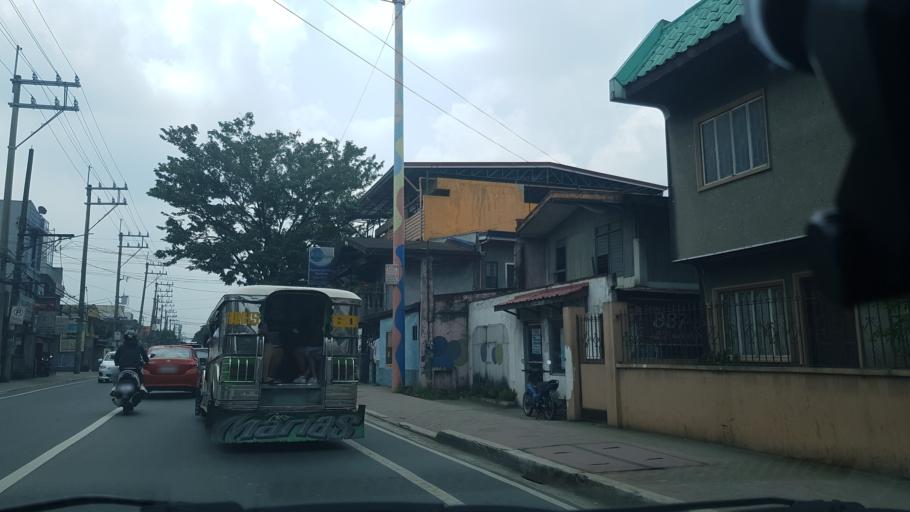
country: PH
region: Calabarzon
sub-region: Province of Rizal
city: San Mateo
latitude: 14.6721
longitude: 121.1091
